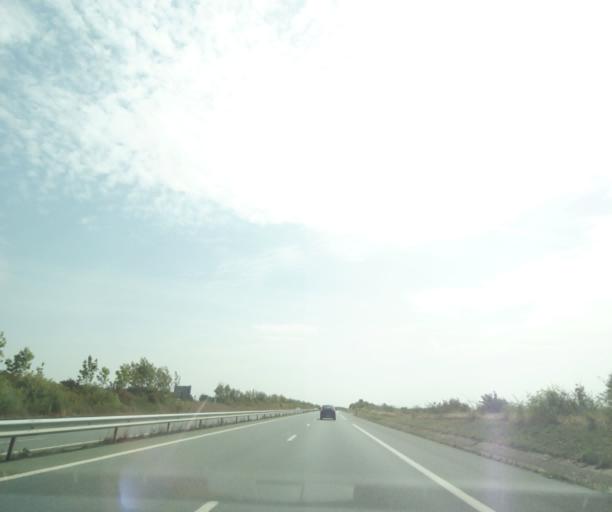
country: FR
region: Poitou-Charentes
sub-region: Departement des Deux-Sevres
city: Saint-Gelais
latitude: 46.4031
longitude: -0.3835
